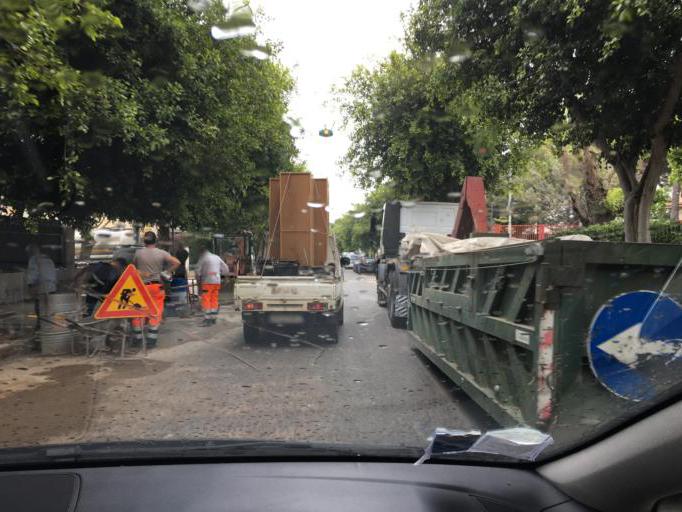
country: IT
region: Sicily
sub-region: Palermo
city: Palermo
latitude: 38.1969
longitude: 13.3158
